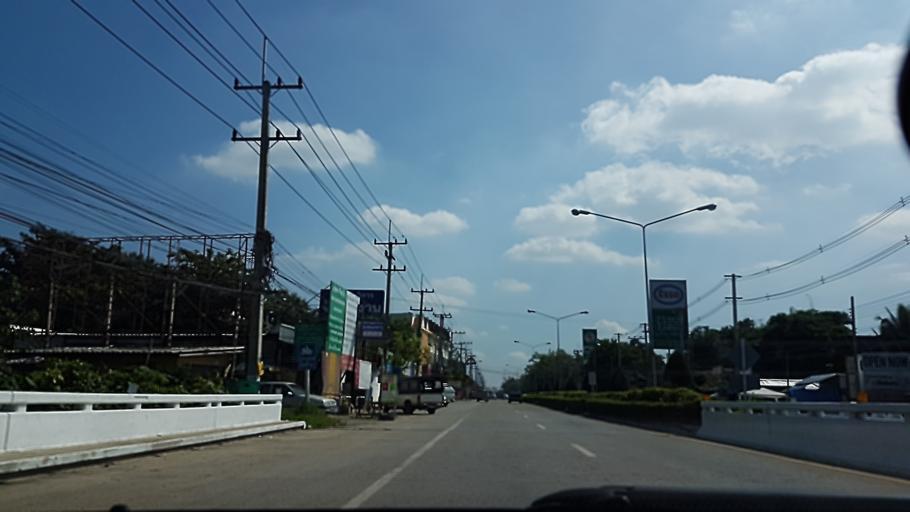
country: TH
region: Chiang Mai
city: Chiang Mai
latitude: 18.8362
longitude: 98.9753
